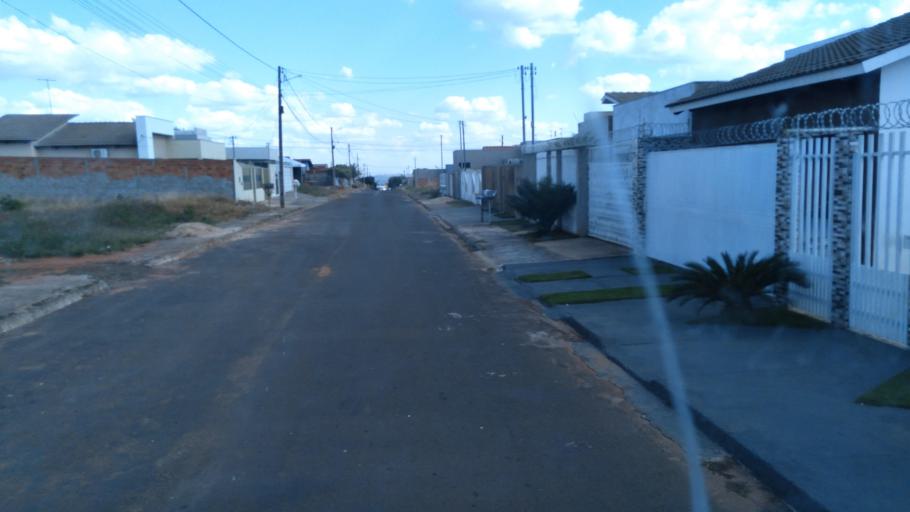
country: YE
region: Al Mahrah
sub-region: Shahan
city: Shihan as Sufla
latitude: 17.5428
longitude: 52.5393
